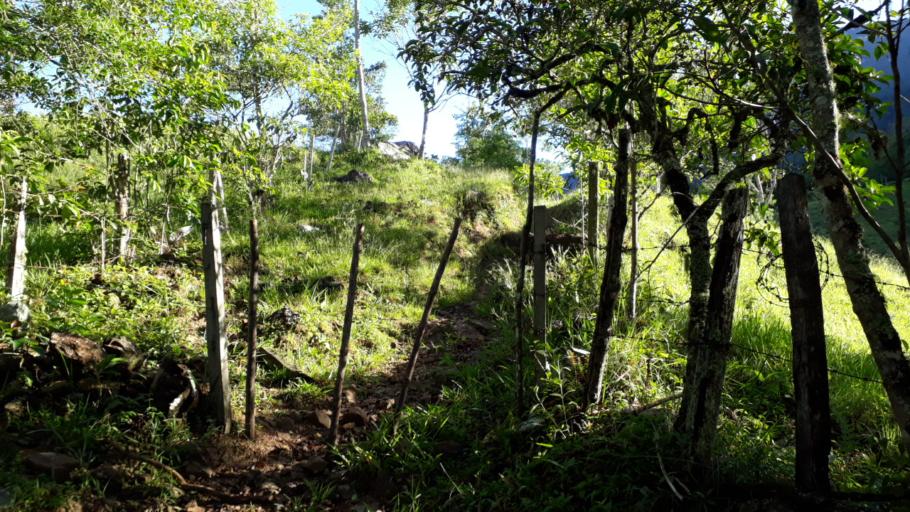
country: CO
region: Casanare
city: Nunchia
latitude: 5.6366
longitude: -72.4260
